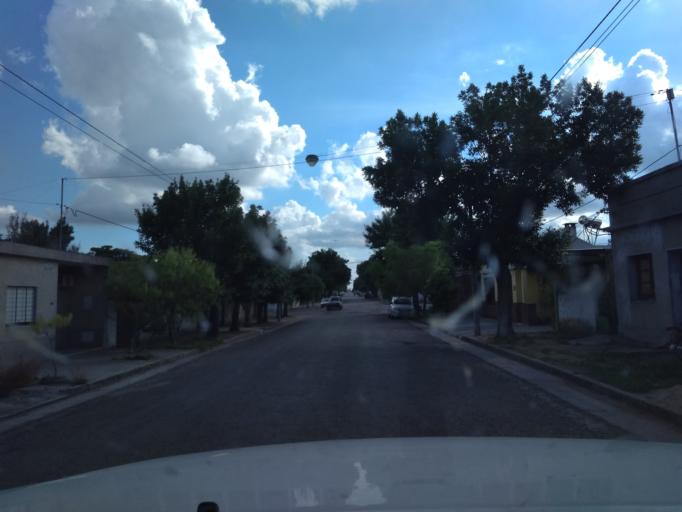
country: UY
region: Florida
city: Florida
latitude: -34.0902
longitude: -56.2167
